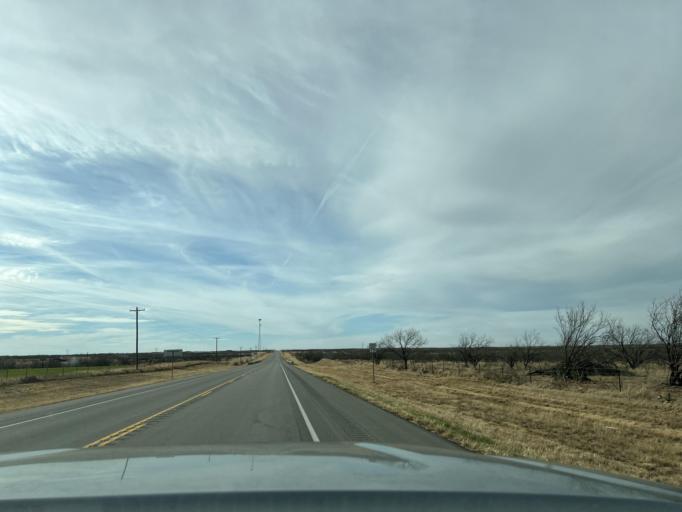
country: US
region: Texas
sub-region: Jones County
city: Anson
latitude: 32.7507
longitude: -99.7153
